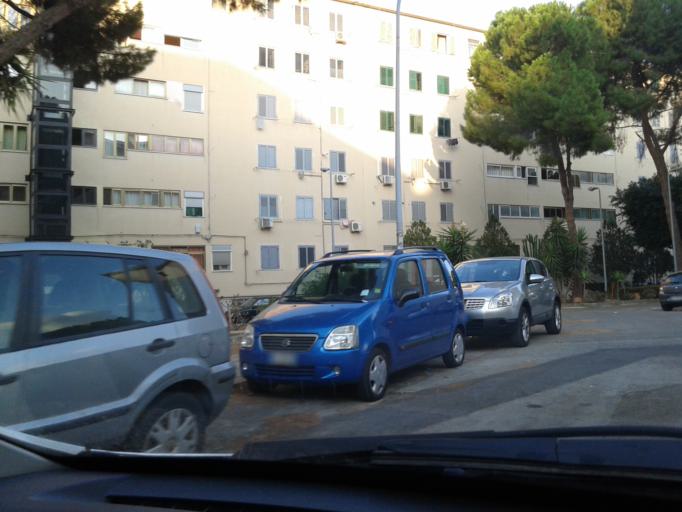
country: IT
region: Sicily
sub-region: Palermo
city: Palermo
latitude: 38.1015
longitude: 13.3367
